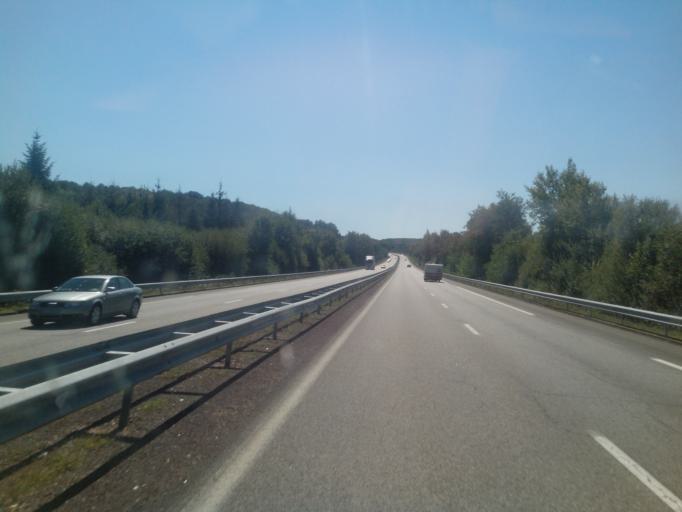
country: FR
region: Brittany
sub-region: Departement du Morbihan
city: Malestroit
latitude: 47.8344
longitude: -2.4294
